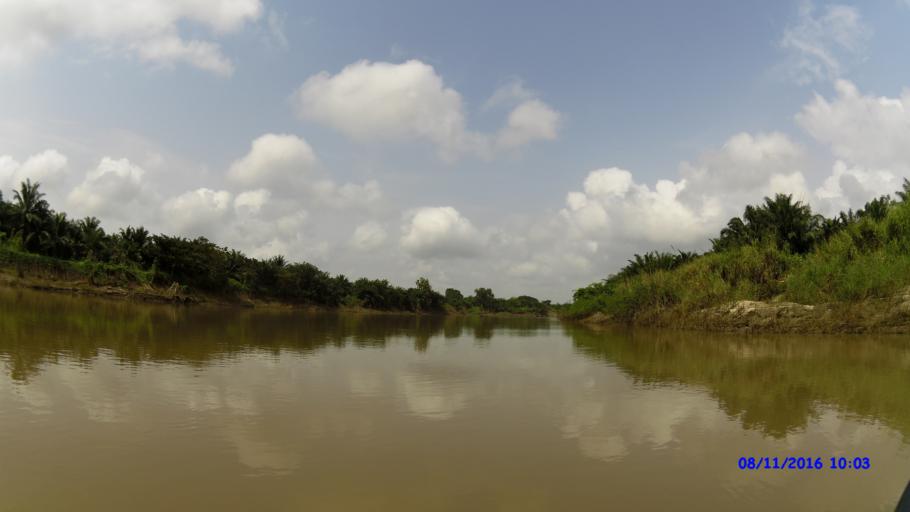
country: BJ
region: Mono
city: Come
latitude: 6.4411
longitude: 1.7595
